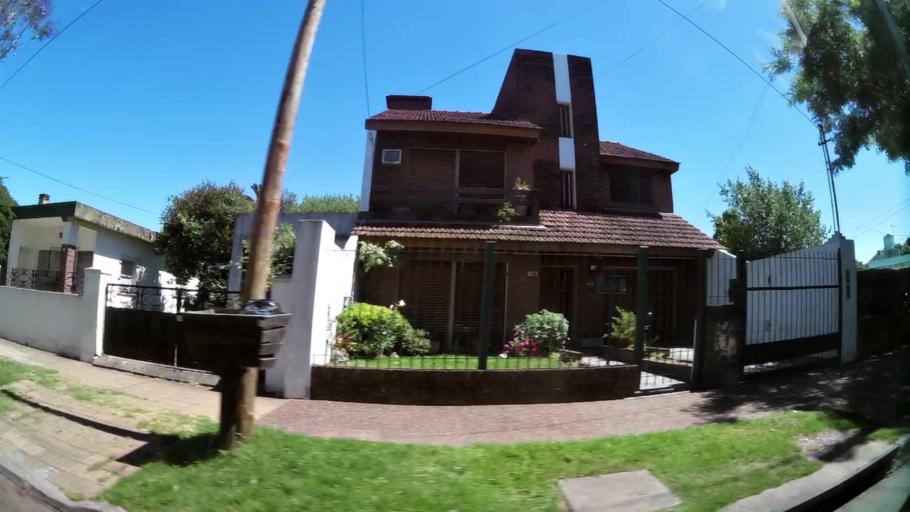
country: AR
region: Buenos Aires
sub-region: Partido de San Isidro
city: San Isidro
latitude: -34.4737
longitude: -58.5301
